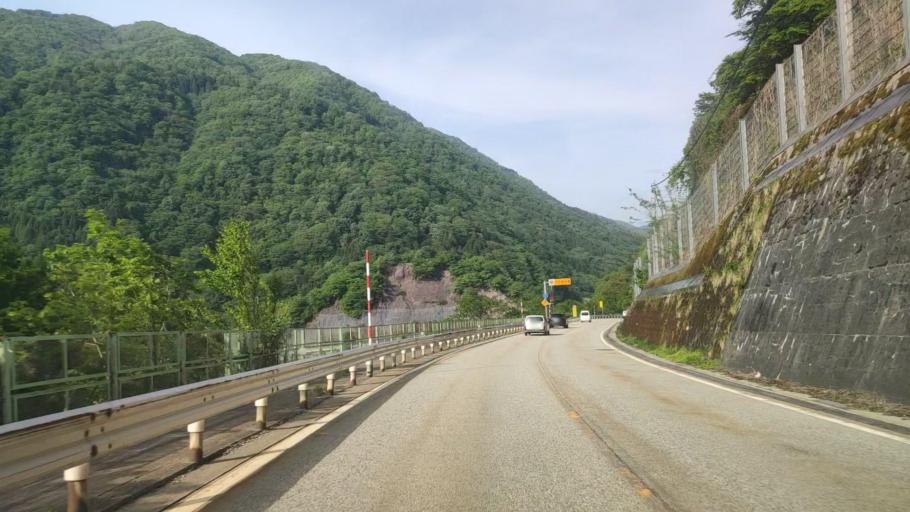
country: JP
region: Toyama
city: Yatsuomachi-higashikumisaka
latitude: 36.4040
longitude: 137.2942
